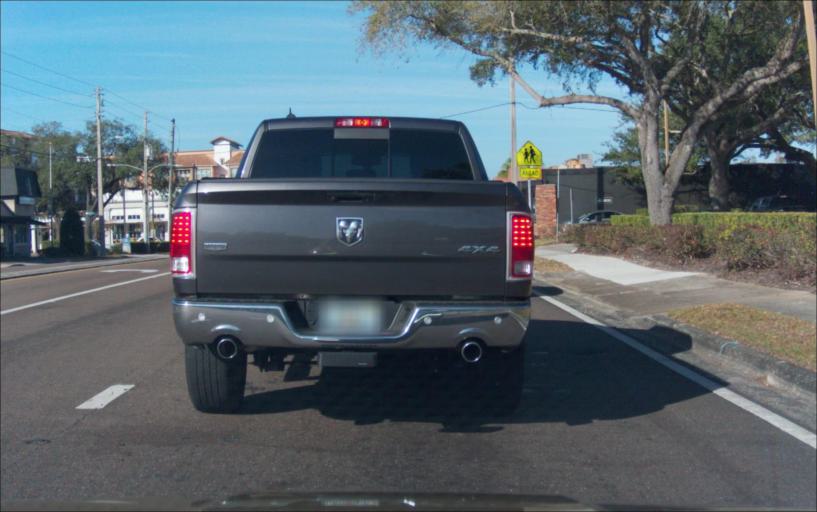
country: US
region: Florida
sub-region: Orange County
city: Maitland
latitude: 28.6353
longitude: -81.3656
